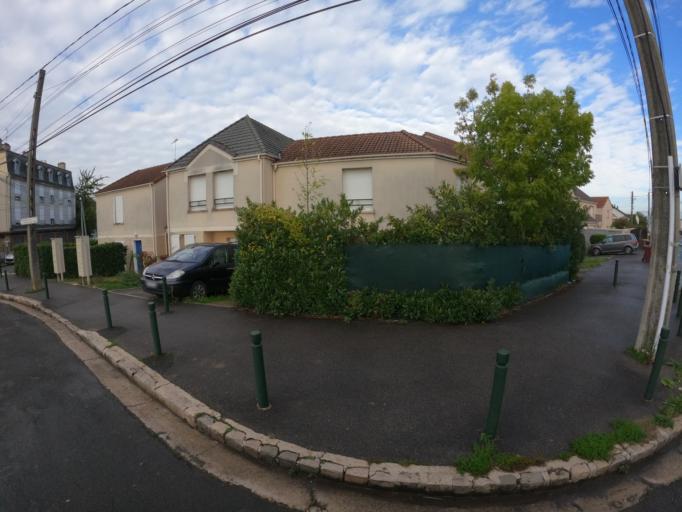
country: FR
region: Ile-de-France
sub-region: Departement de Seine-et-Marne
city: Courtry
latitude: 48.8991
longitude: 2.6026
